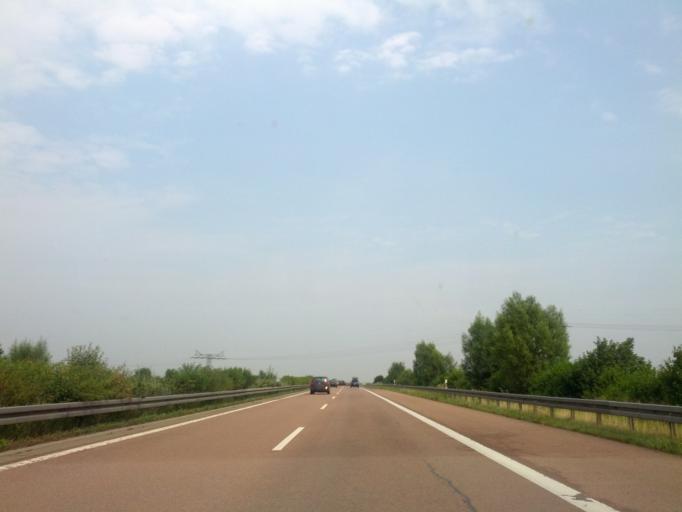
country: DE
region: Mecklenburg-Vorpommern
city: Broderstorf
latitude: 54.0321
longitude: 12.3025
